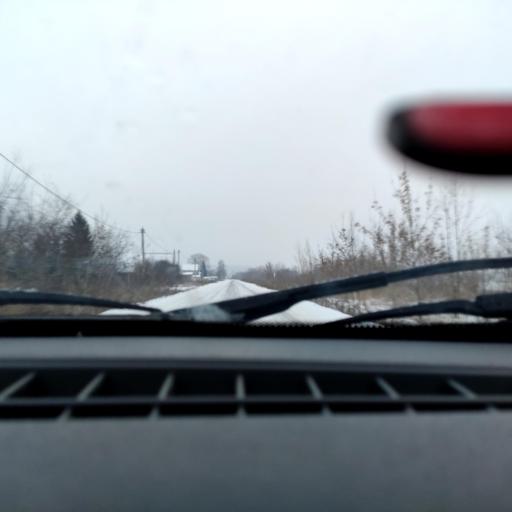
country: RU
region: Bashkortostan
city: Blagoveshchensk
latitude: 54.9026
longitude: 56.0129
